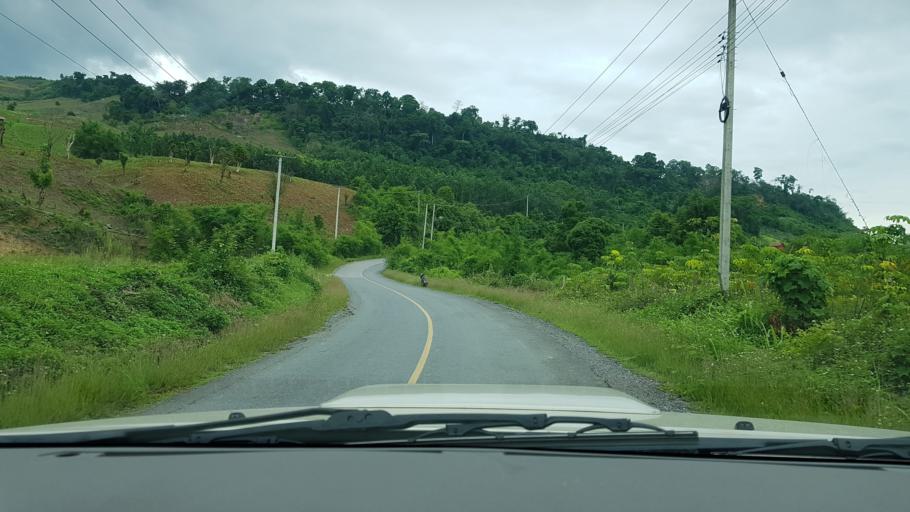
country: LA
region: Loungnamtha
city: Muang Nale
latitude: 20.1808
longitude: 101.5190
